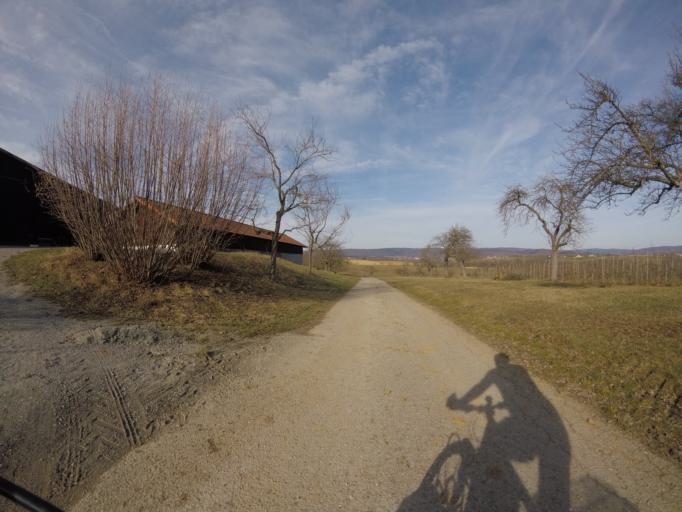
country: DE
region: Baden-Wuerttemberg
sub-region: Regierungsbezirk Stuttgart
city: Mittelschontal
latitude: 48.9499
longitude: 9.3887
